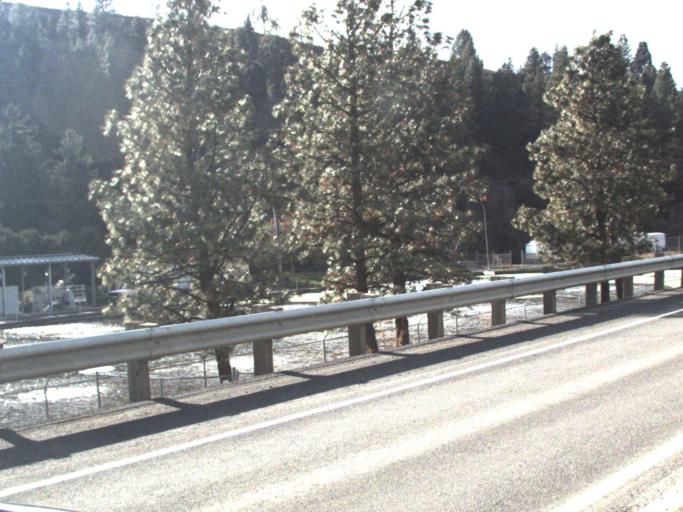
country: US
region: Washington
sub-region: Whitman County
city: Colfax
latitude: 46.8910
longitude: -117.3719
